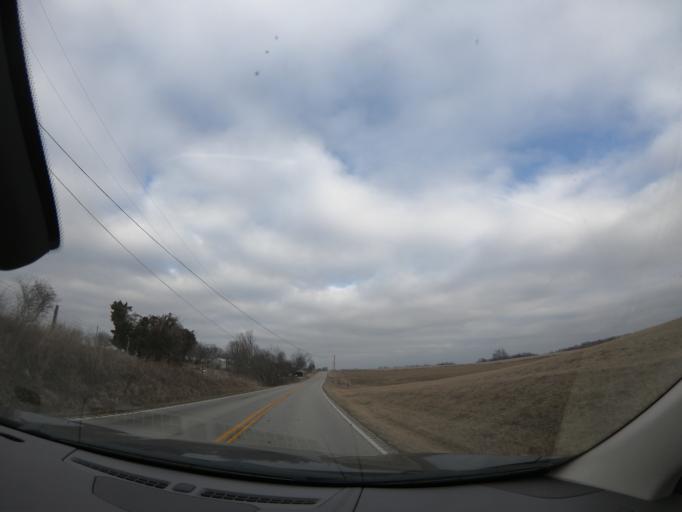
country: US
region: Kentucky
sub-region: Nelson County
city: Bardstown
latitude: 37.8661
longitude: -85.3296
